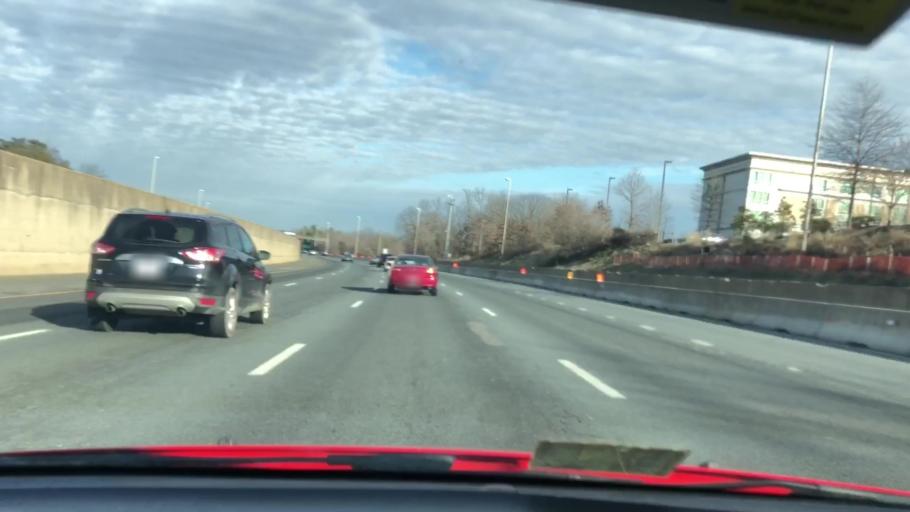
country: US
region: Virginia
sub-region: Prince William County
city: Sudley
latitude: 38.8029
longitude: -77.5109
